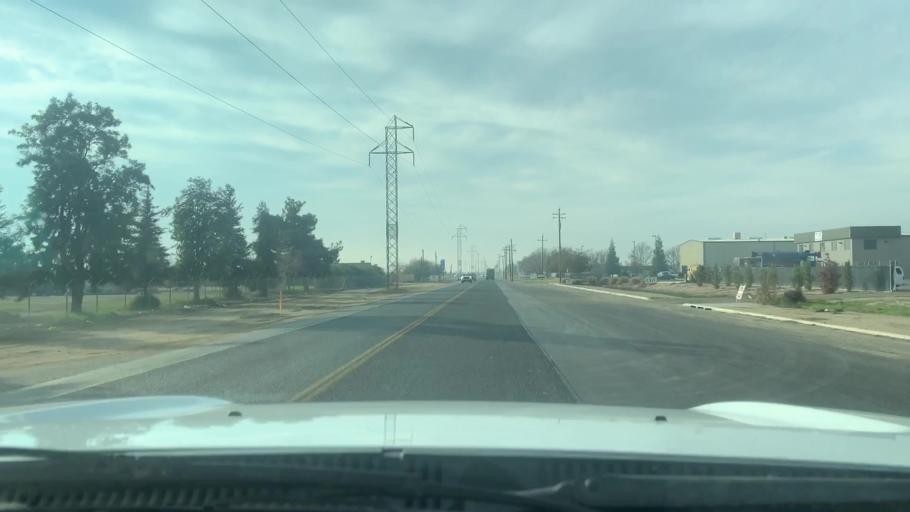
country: US
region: California
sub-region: Kern County
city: Shafter
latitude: 35.4417
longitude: -119.2464
